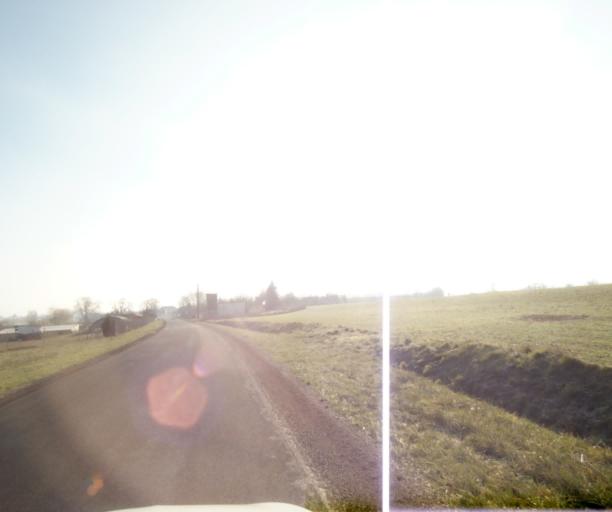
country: FR
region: Champagne-Ardenne
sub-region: Departement de la Haute-Marne
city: Montier-en-Der
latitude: 48.4843
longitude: 4.7446
